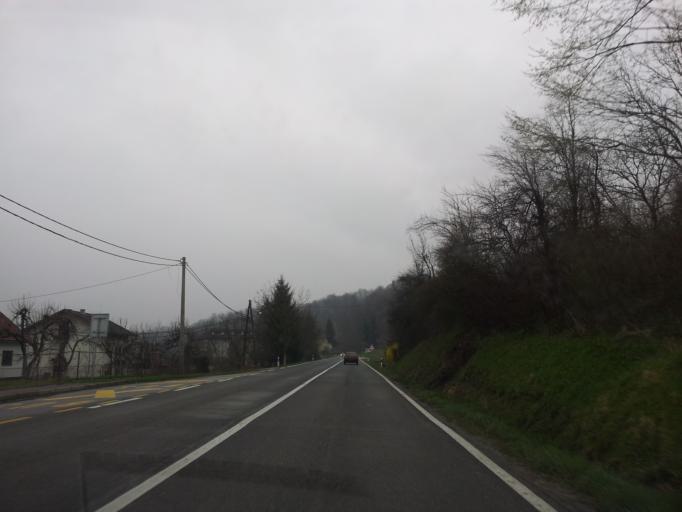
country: HR
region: Karlovacka
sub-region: Grad Karlovac
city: Karlovac
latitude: 45.4033
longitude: 15.6129
